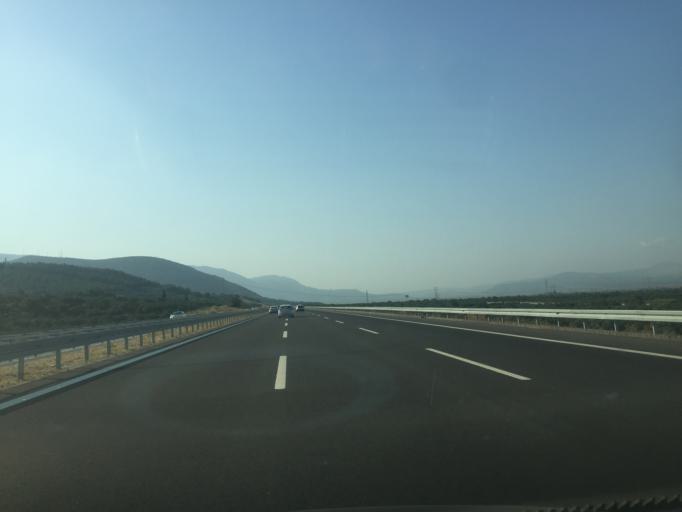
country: TR
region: Manisa
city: Zeytinliova
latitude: 39.0504
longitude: 27.7333
